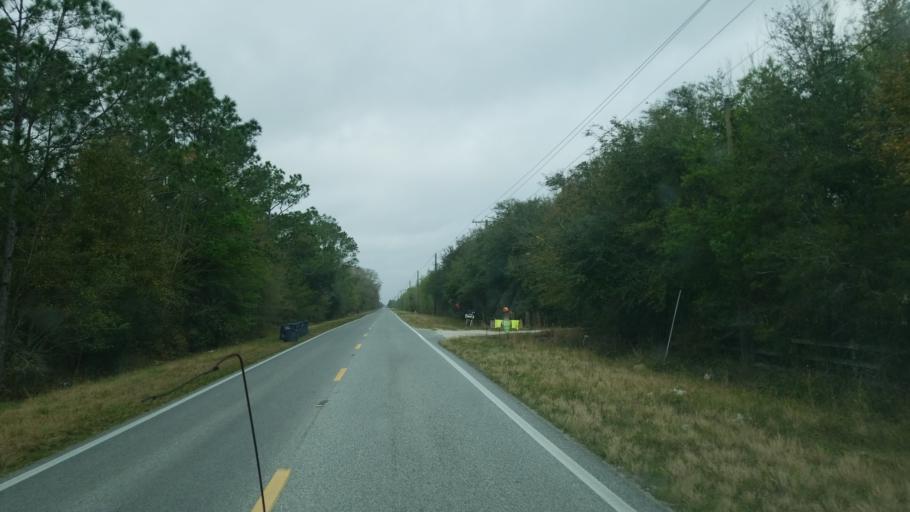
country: US
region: Florida
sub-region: Polk County
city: Polk City
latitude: 28.2590
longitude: -81.8977
